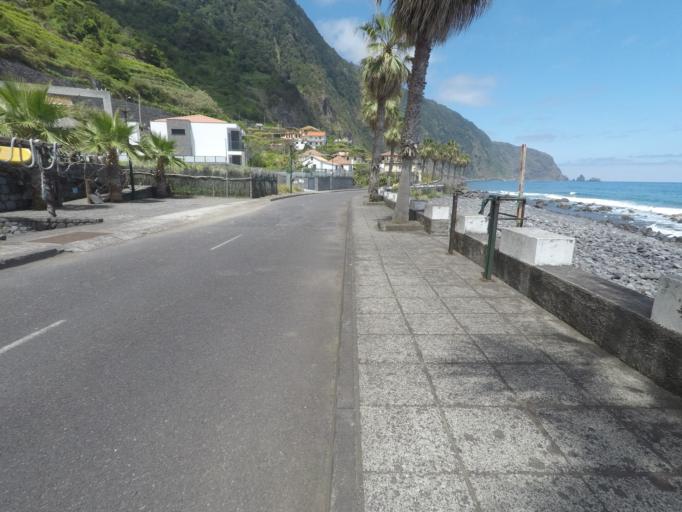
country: PT
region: Madeira
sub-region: Porto Moniz
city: Porto Moniz
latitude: 32.8258
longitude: -17.1179
